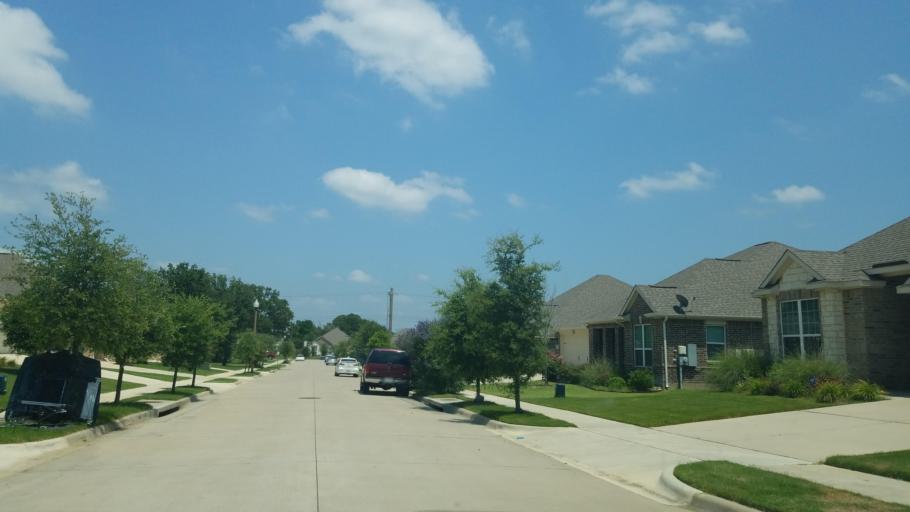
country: US
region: Texas
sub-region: Denton County
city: Denton
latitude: 33.2227
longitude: -97.1036
